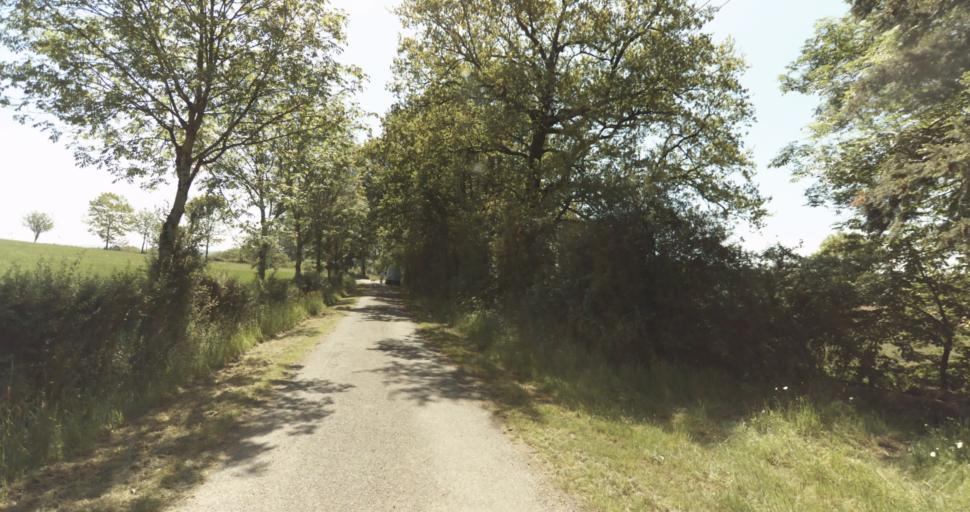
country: FR
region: Limousin
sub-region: Departement de la Haute-Vienne
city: Le Vigen
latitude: 45.7329
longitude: 1.2940
